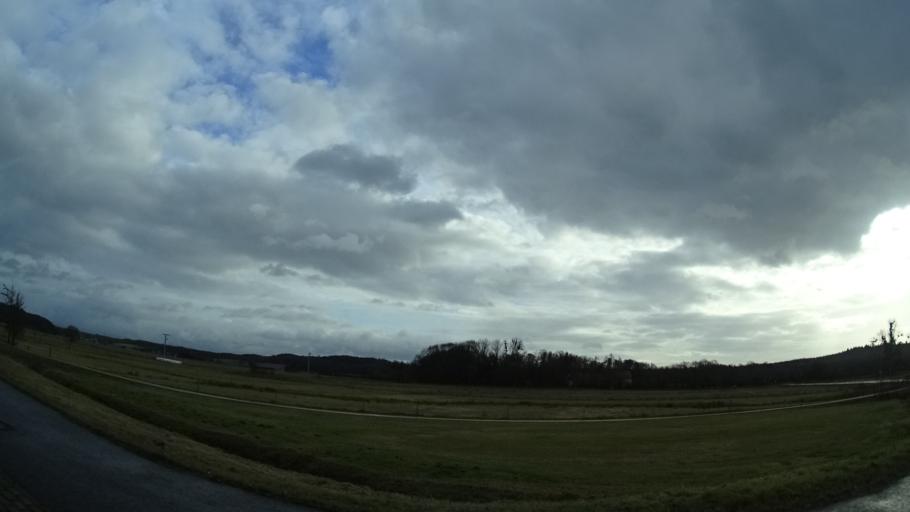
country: DE
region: Hesse
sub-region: Regierungsbezirk Giessen
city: Hungen
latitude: 50.5367
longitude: 8.8832
